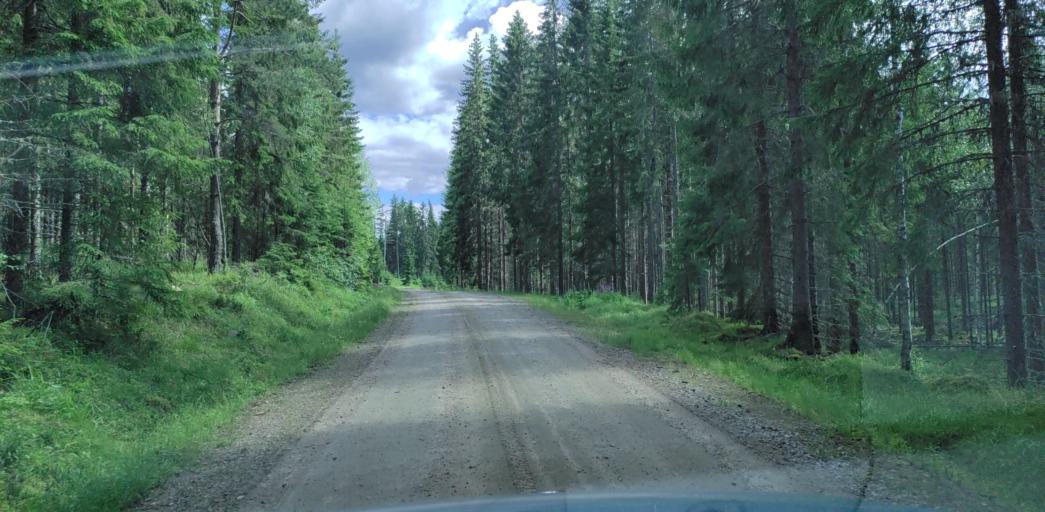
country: SE
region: Vaermland
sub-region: Hagfors Kommun
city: Ekshaerad
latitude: 60.0612
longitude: 13.3071
